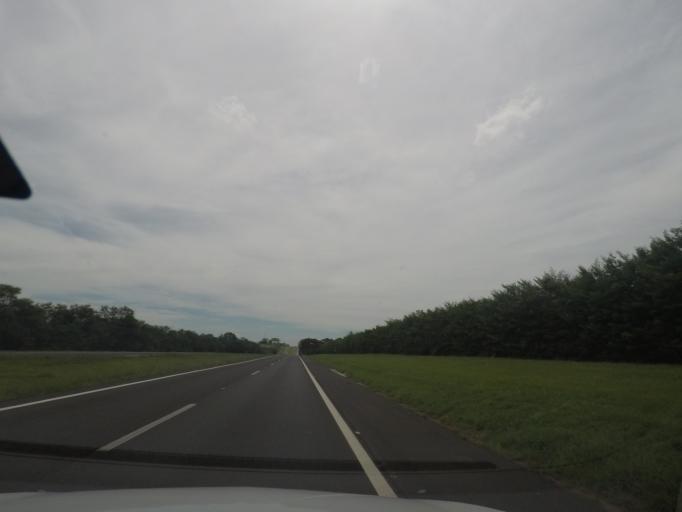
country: BR
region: Sao Paulo
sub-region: Bebedouro
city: Bebedouro
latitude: -20.9767
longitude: -48.4381
